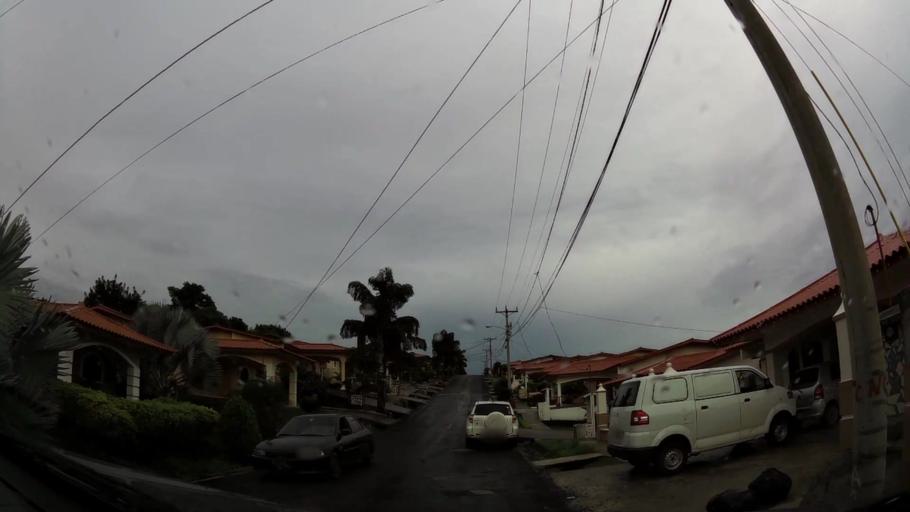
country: PA
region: Veraguas
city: Santiago de Veraguas
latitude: 8.0865
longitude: -80.9879
